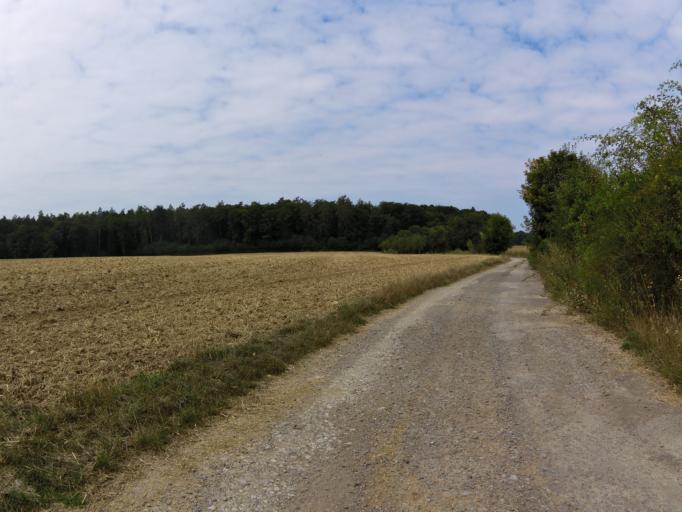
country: DE
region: Bavaria
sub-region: Regierungsbezirk Unterfranken
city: Kleinrinderfeld
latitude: 49.7024
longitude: 9.8326
